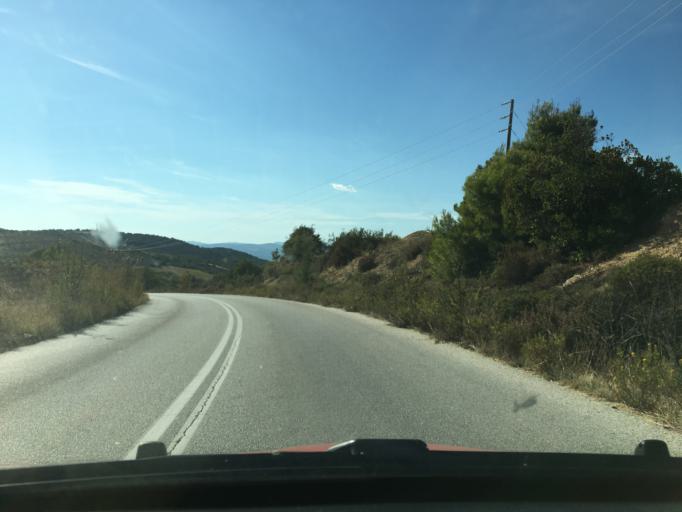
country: GR
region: Central Macedonia
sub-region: Nomos Chalkidikis
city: Megali Panagia
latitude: 40.3832
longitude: 23.7323
